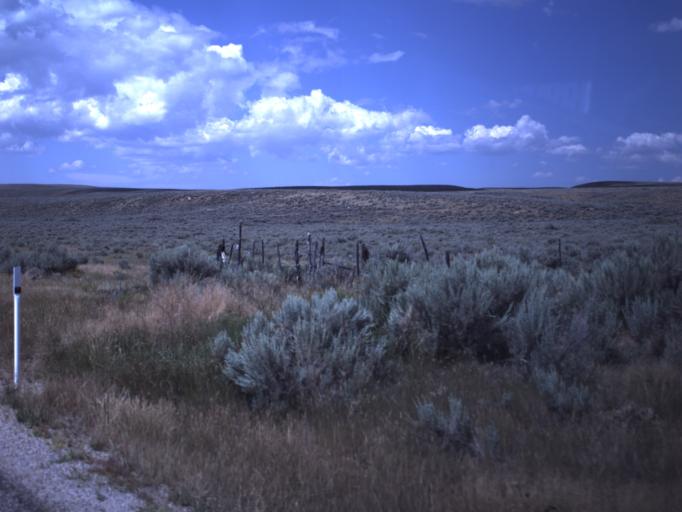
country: US
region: Utah
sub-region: Rich County
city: Randolph
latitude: 41.7719
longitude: -111.1292
